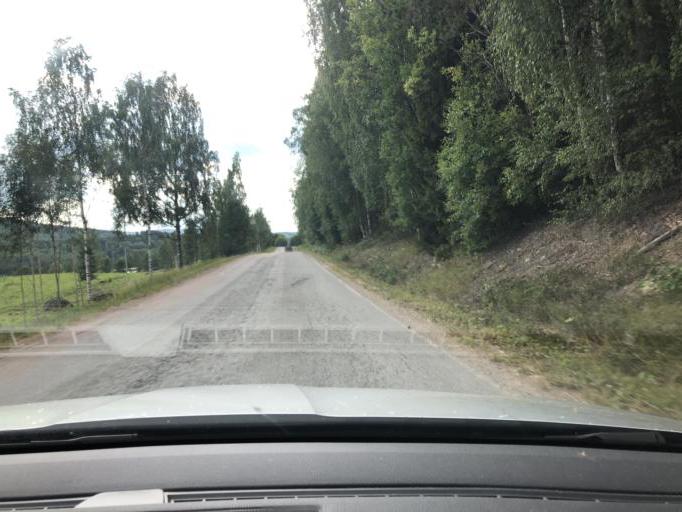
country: SE
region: Vaesternorrland
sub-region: Solleftea Kommun
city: Solleftea
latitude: 63.2056
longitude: 17.1513
